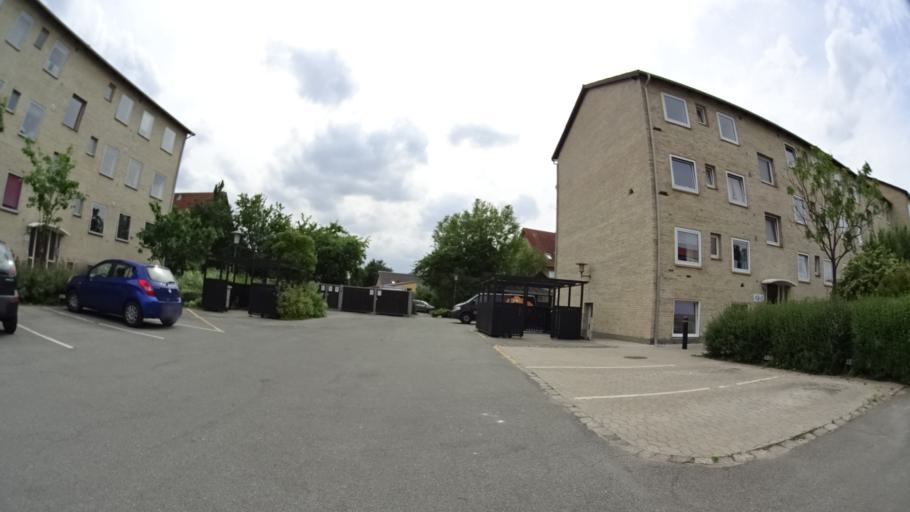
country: DK
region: Central Jutland
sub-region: Arhus Kommune
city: Stavtrup
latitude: 56.1485
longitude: 10.1565
